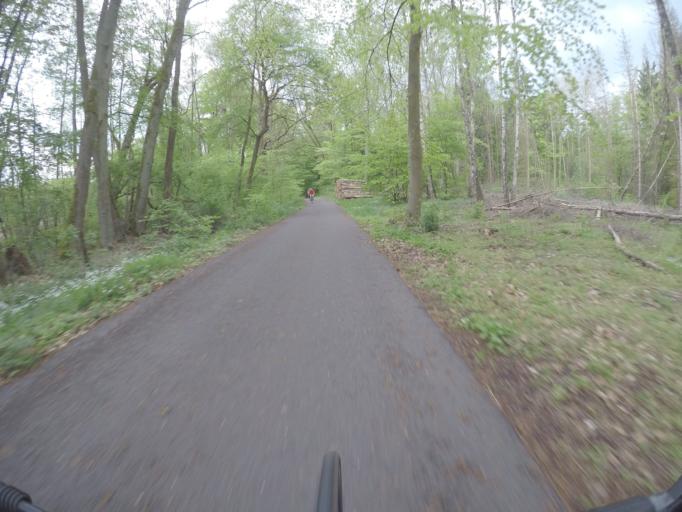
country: DE
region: Brandenburg
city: Marienwerder
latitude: 52.8569
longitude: 13.6122
